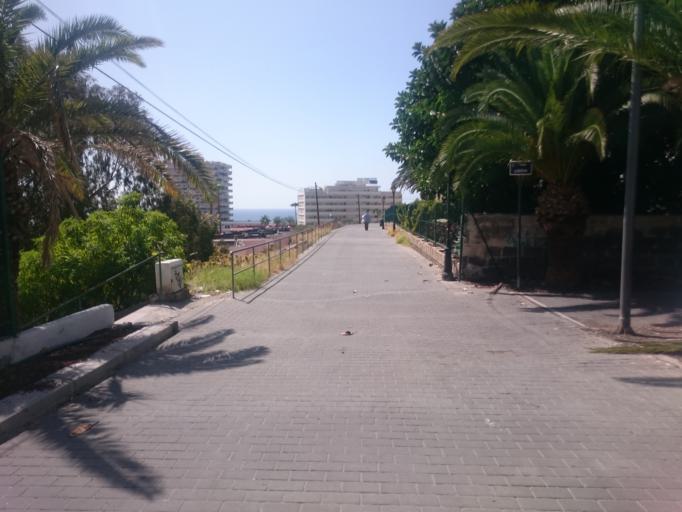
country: ES
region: Canary Islands
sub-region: Provincia de Santa Cruz de Tenerife
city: Playa de las Americas
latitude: 28.0508
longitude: -16.7111
